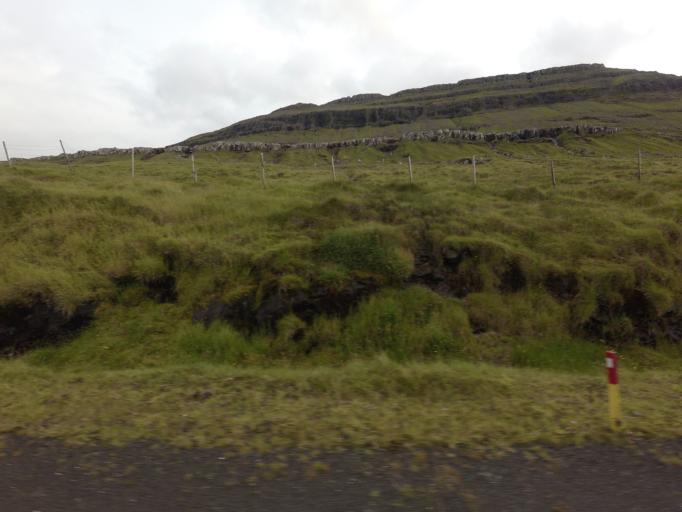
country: FO
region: Streymoy
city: Kollafjordhur
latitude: 62.1409
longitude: -6.8974
